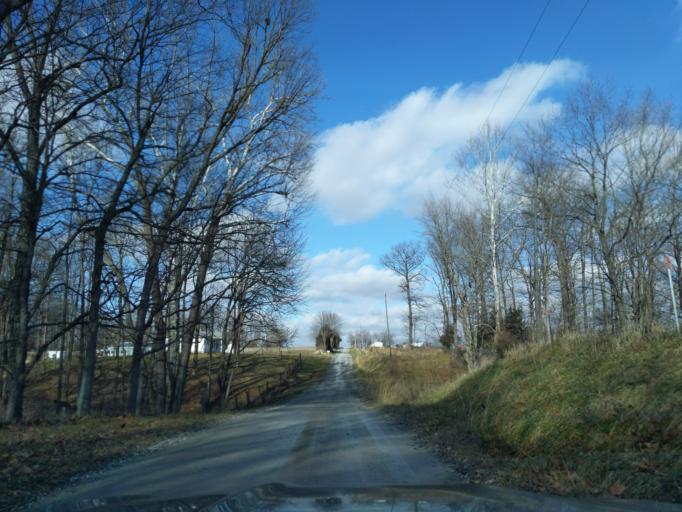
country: US
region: Indiana
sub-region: Decatur County
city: Greensburg
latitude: 39.2592
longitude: -85.4842
